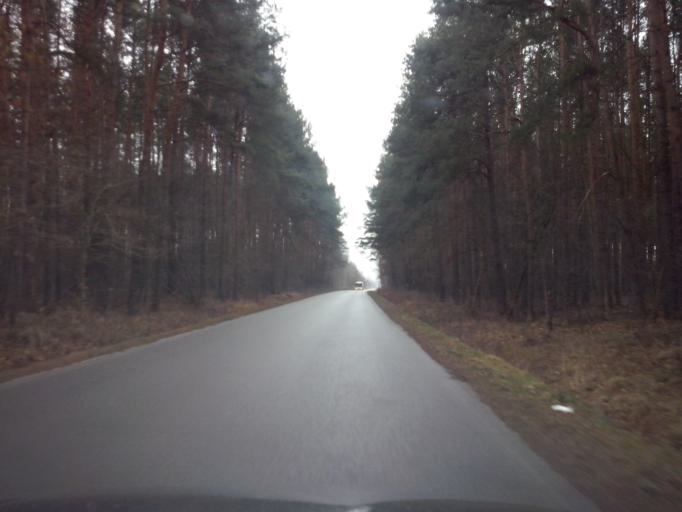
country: PL
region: Subcarpathian Voivodeship
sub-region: Powiat nizanski
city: Bieliny
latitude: 50.4583
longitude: 22.2834
